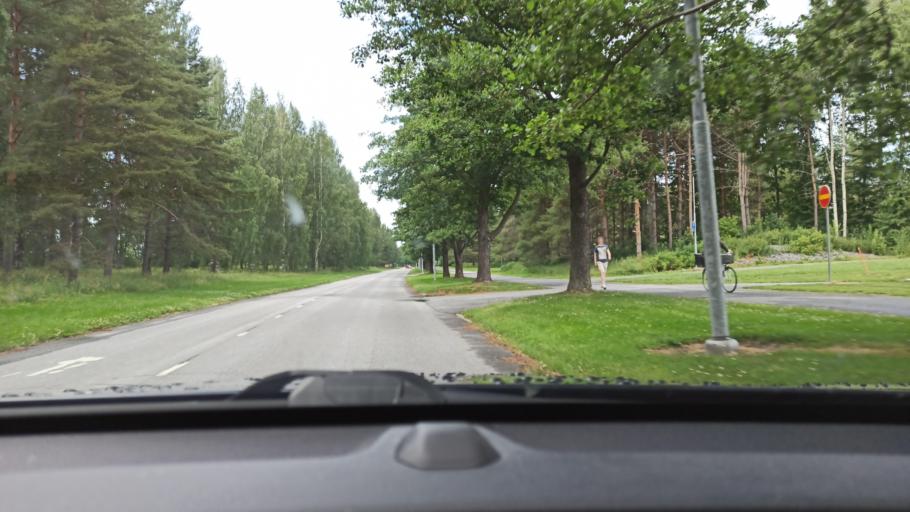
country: FI
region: Satakunta
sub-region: Pori
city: Pori
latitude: 61.4994
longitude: 21.7853
